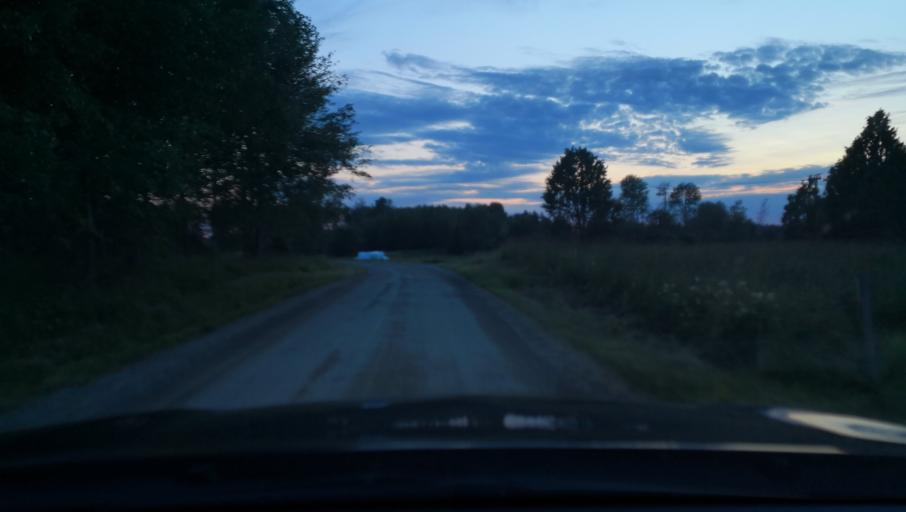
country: SE
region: Uppsala
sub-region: Osthammars Kommun
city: Bjorklinge
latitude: 60.0029
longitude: 17.3518
